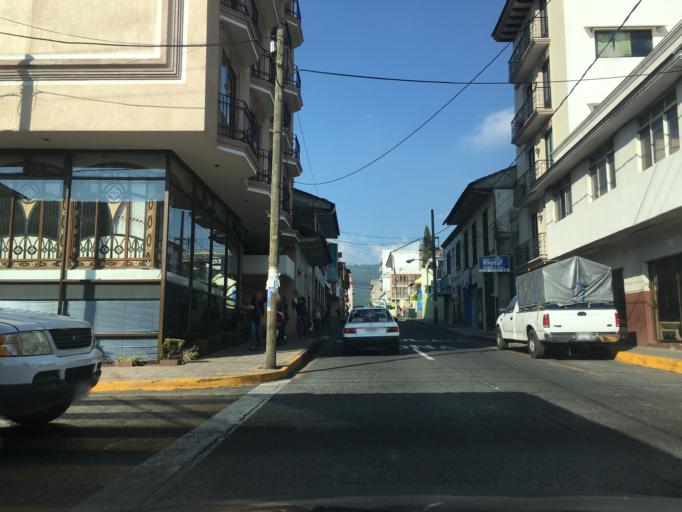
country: MX
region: Michoacan
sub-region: Uruapan
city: Uruapan
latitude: 19.4183
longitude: -102.0624
